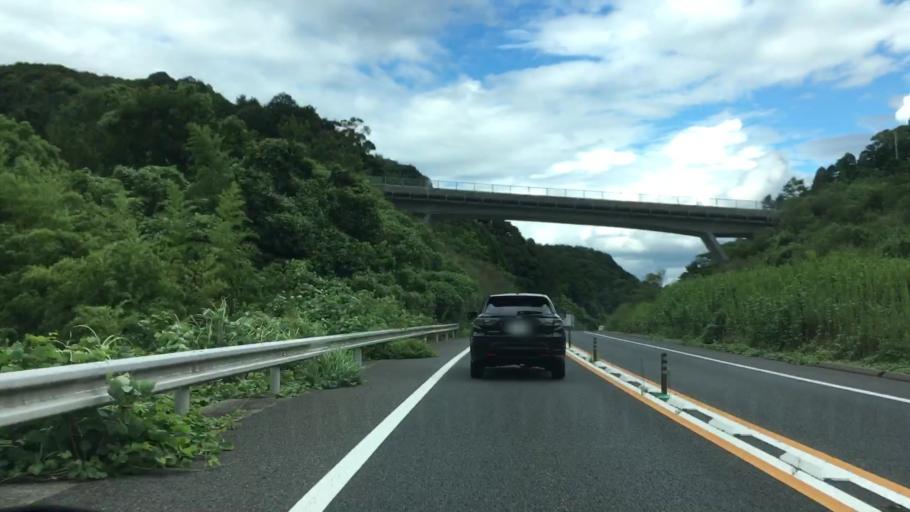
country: JP
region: Saga Prefecture
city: Karatsu
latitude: 33.3987
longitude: 129.9377
